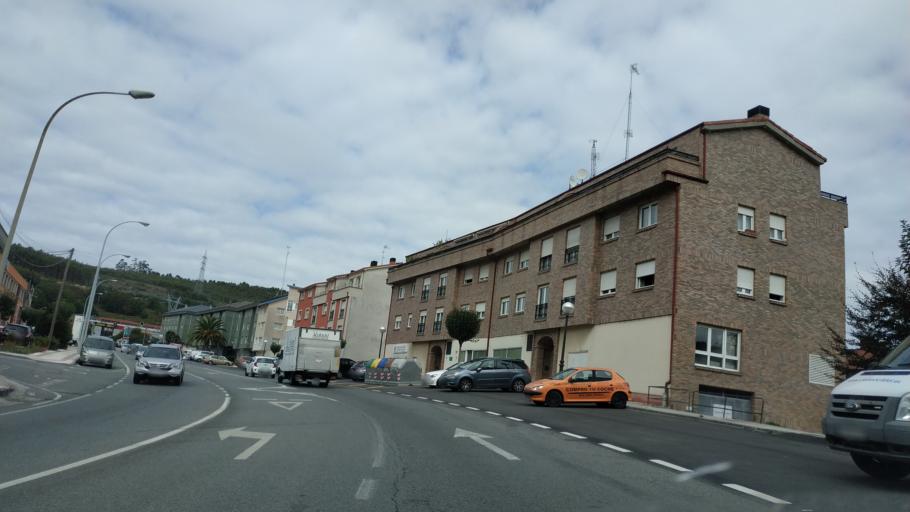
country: ES
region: Galicia
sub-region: Provincia da Coruna
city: Arteixo
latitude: 43.3213
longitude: -8.4738
